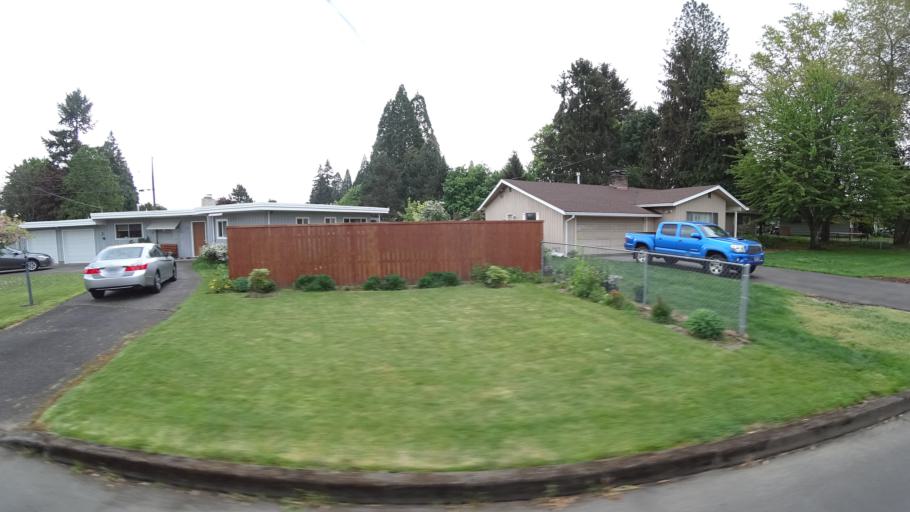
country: US
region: Oregon
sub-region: Washington County
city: Hillsboro
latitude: 45.5291
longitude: -122.9807
